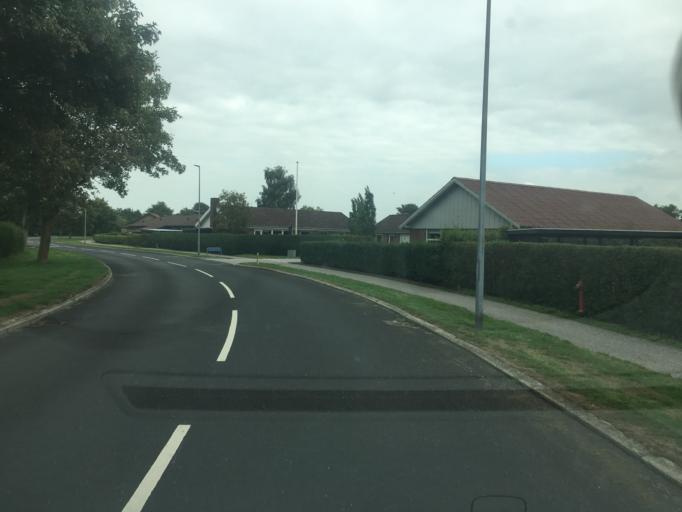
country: DK
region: South Denmark
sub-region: Tonder Kommune
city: Tonder
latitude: 54.9343
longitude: 8.8489
